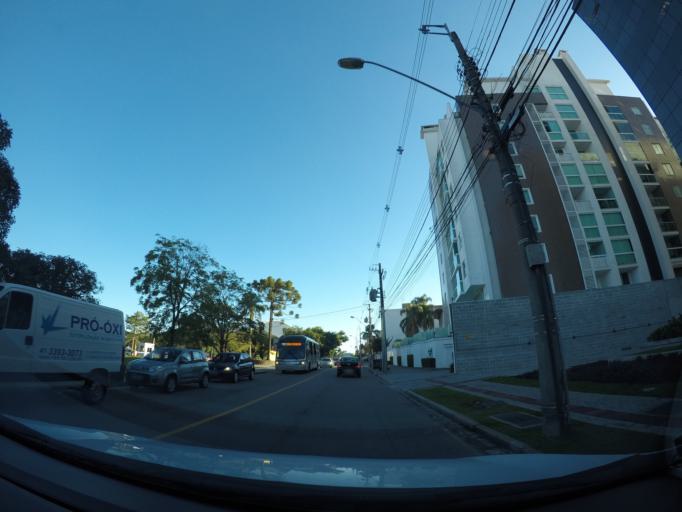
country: BR
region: Parana
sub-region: Curitiba
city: Curitiba
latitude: -25.4116
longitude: -49.2658
